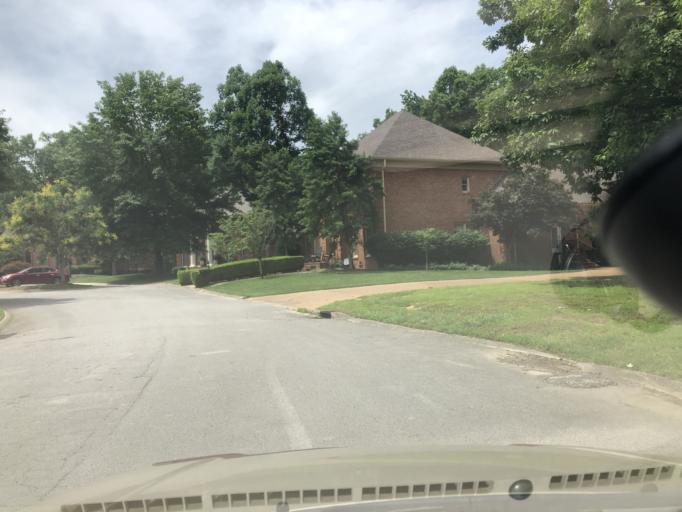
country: US
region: Tennessee
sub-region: Davidson County
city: Lakewood
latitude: 36.2602
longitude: -86.5865
